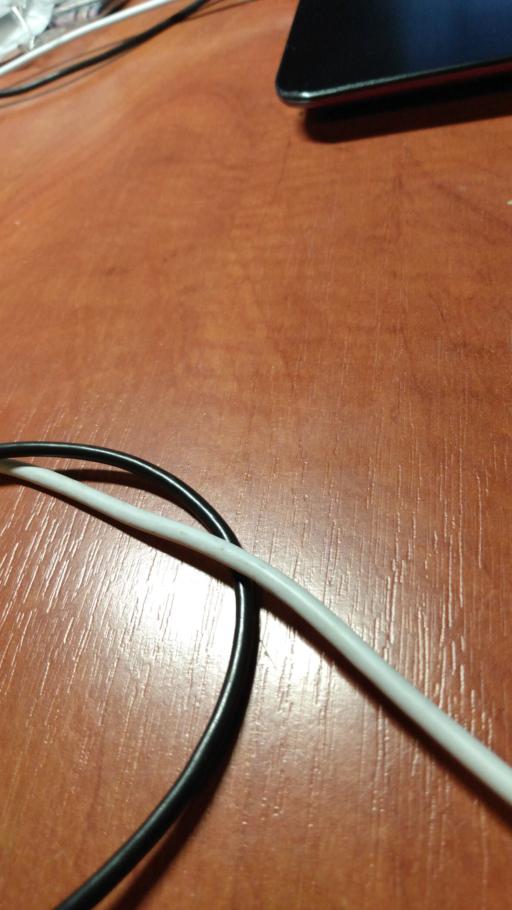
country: RU
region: Republic of Karelia
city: Pudozh
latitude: 62.0692
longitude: 37.5745
